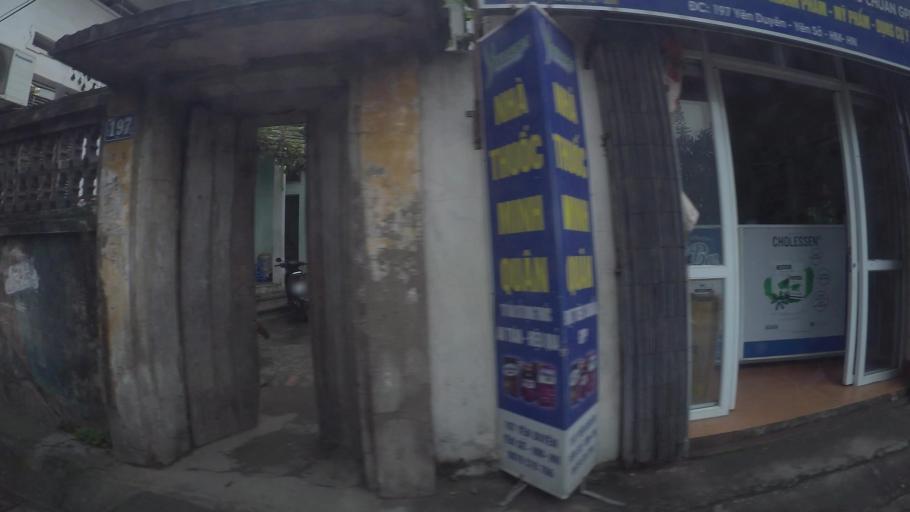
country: VN
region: Ha Noi
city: Van Dien
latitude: 20.9691
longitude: 105.8712
